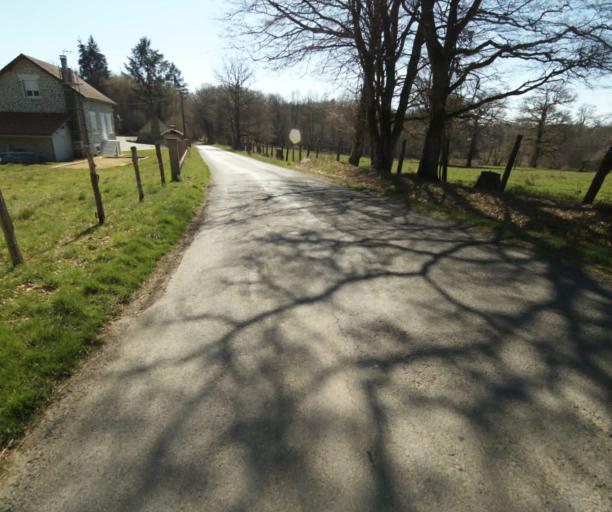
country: FR
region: Limousin
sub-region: Departement de la Correze
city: Saint-Clement
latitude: 45.3427
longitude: 1.6421
